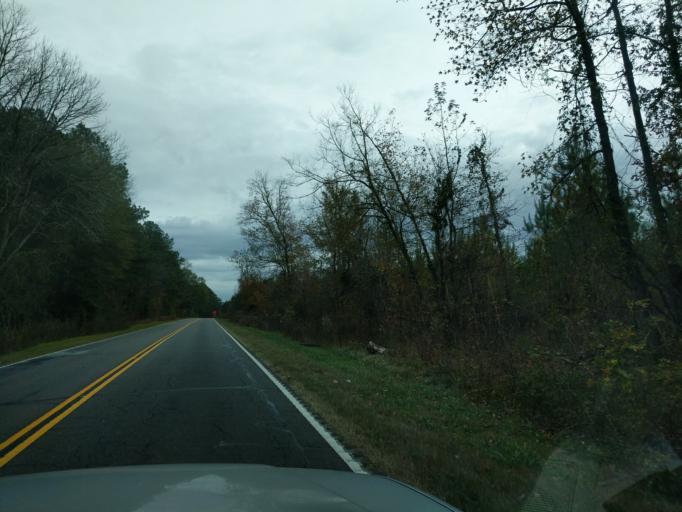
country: US
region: South Carolina
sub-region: Lexington County
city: Batesburg
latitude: 33.9450
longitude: -81.6223
